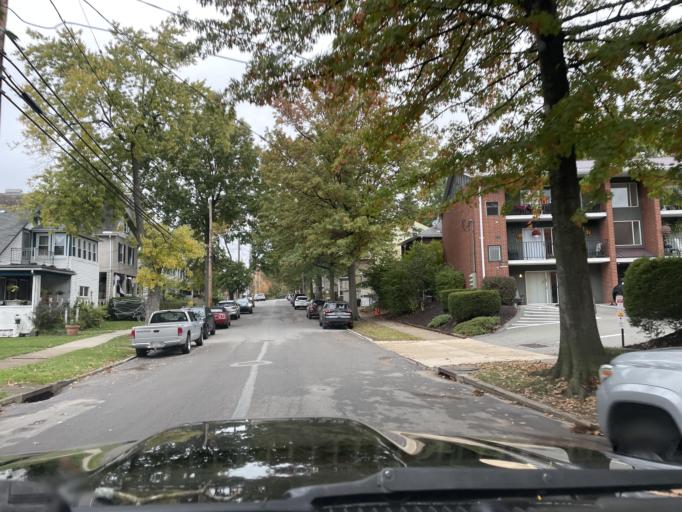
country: US
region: Pennsylvania
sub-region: Allegheny County
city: Oakmont
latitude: 40.5219
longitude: -79.8388
